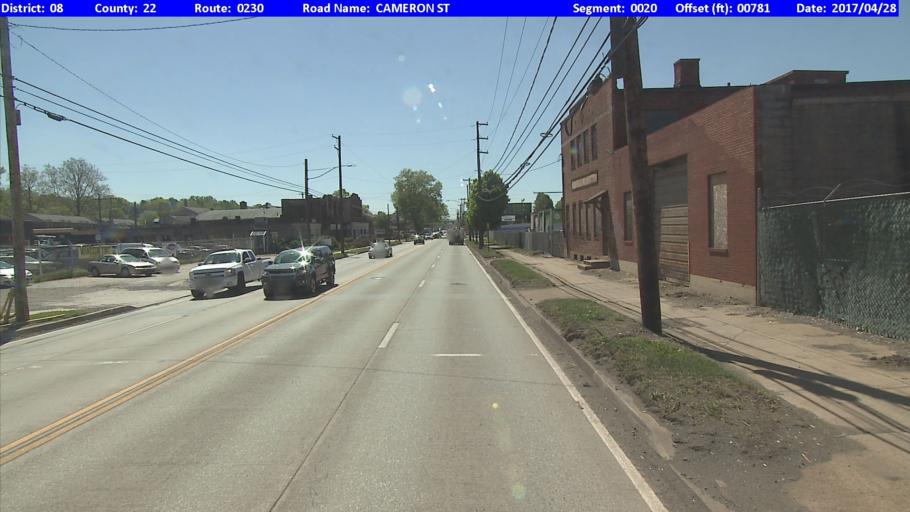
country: US
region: Pennsylvania
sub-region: Dauphin County
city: Harrisburg
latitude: 40.2778
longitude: -76.8792
